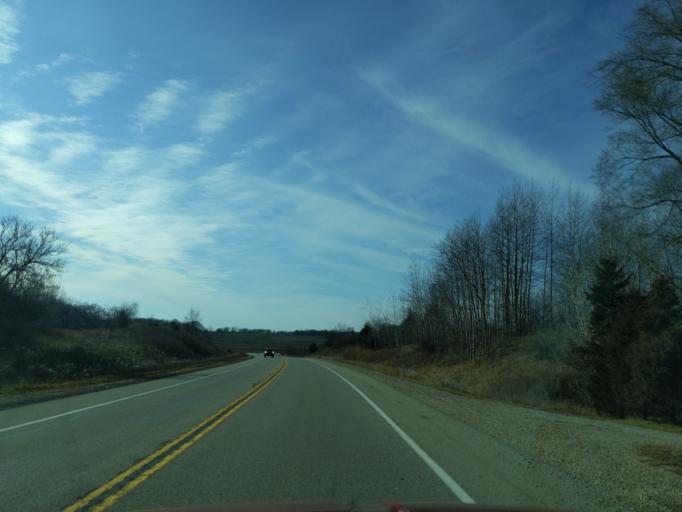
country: US
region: Wisconsin
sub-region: Jefferson County
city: Palmyra
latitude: 42.7985
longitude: -88.6111
